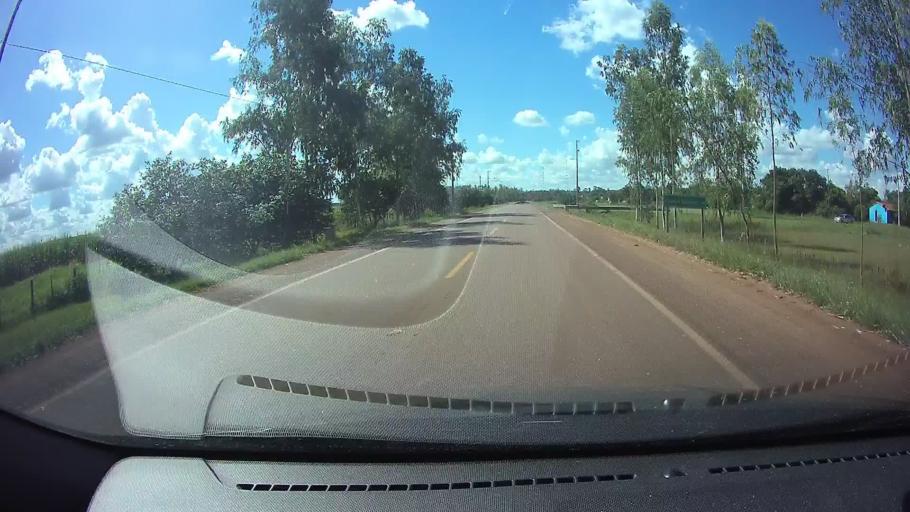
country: PY
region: Guaira
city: Coronel Martinez
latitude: -25.7830
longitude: -56.6491
